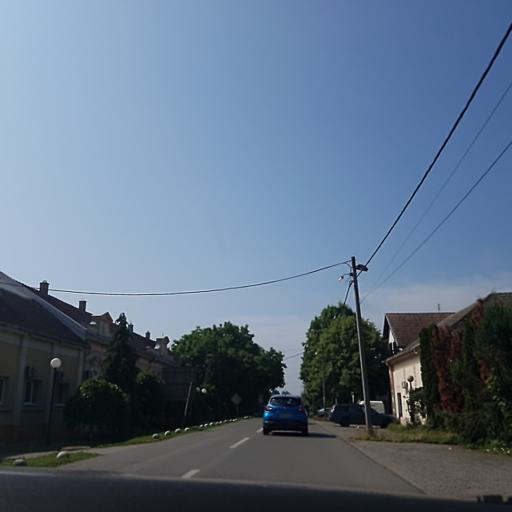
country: RS
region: Autonomna Pokrajina Vojvodina
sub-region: Srednjebanatski Okrug
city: Secanj
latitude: 45.3663
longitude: 20.7724
